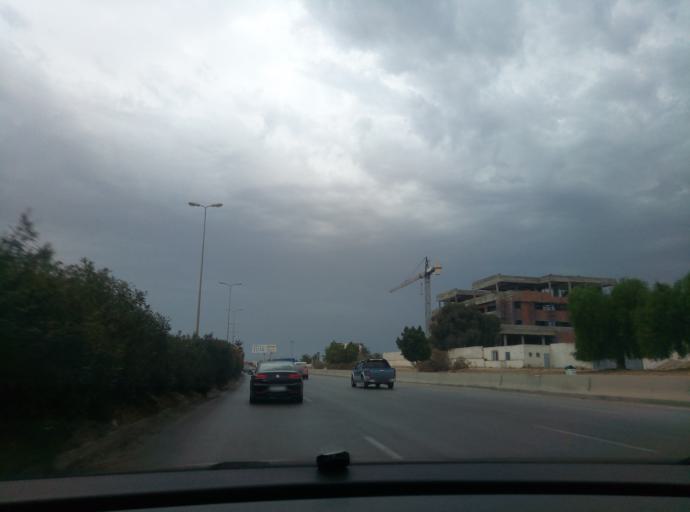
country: TN
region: Bin 'Arus
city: Ben Arous
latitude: 36.7369
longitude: 10.2194
